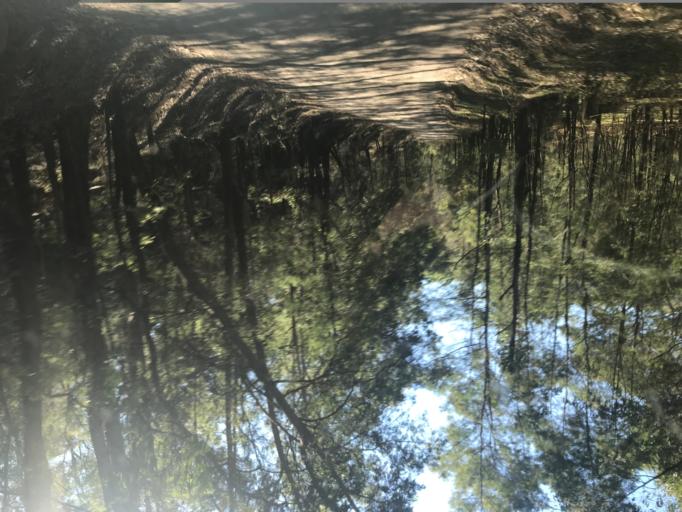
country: AU
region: New South Wales
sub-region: Wyong Shire
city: Little Jilliby
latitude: -33.1966
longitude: 151.0167
